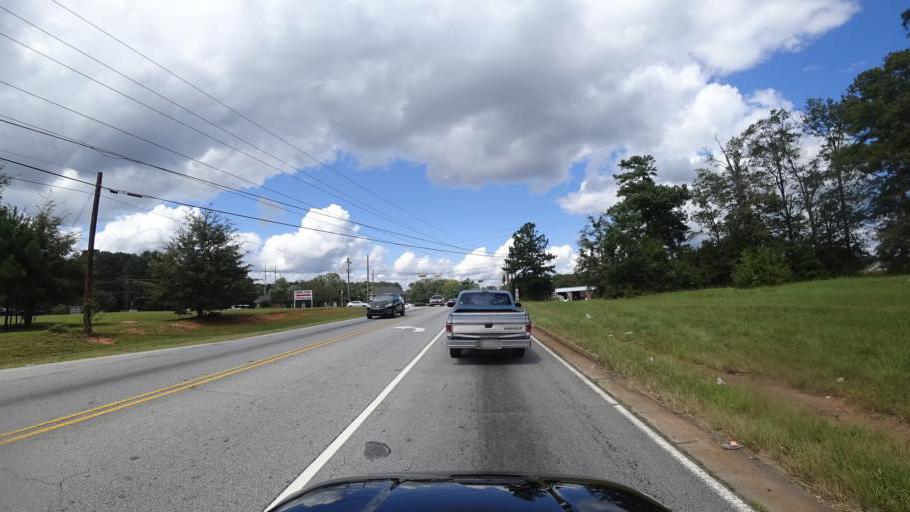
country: US
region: Georgia
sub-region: Newton County
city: Oakwood
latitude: 33.6022
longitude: -83.9724
